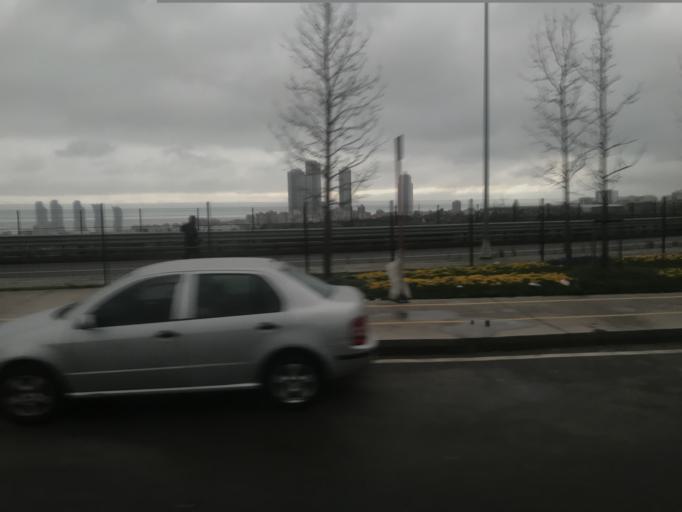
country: TR
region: Istanbul
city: Maltepe
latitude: 40.9085
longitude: 29.2044
